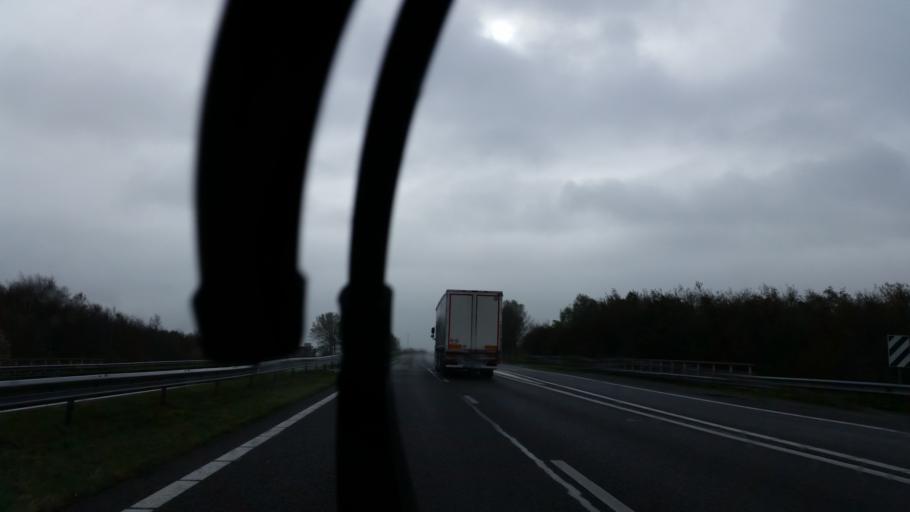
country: NL
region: Friesland
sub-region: Gemeente Boarnsterhim
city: Grou
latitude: 53.0948
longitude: 5.8215
